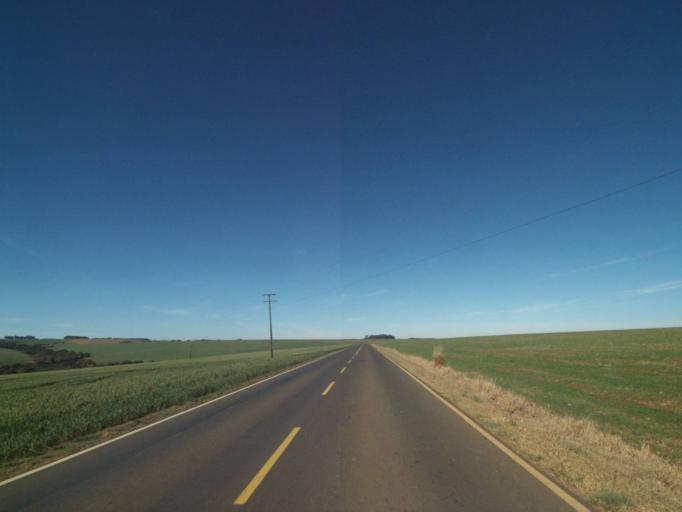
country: BR
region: Parana
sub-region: Tibagi
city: Tibagi
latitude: -24.5577
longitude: -50.2906
